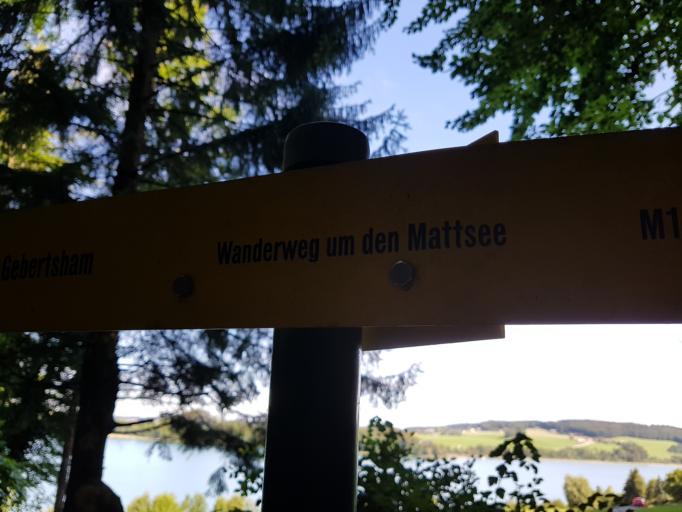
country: AT
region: Salzburg
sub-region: Politischer Bezirk Salzburg-Umgebung
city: Mattsee
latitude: 47.9807
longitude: 13.1286
